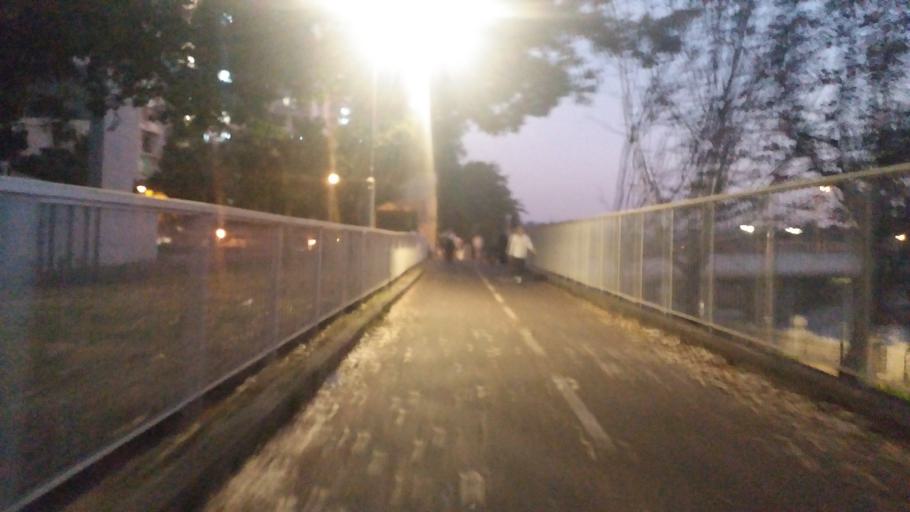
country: HK
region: Yuen Long
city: Yuen Long Kau Hui
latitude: 22.4580
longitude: 113.9950
